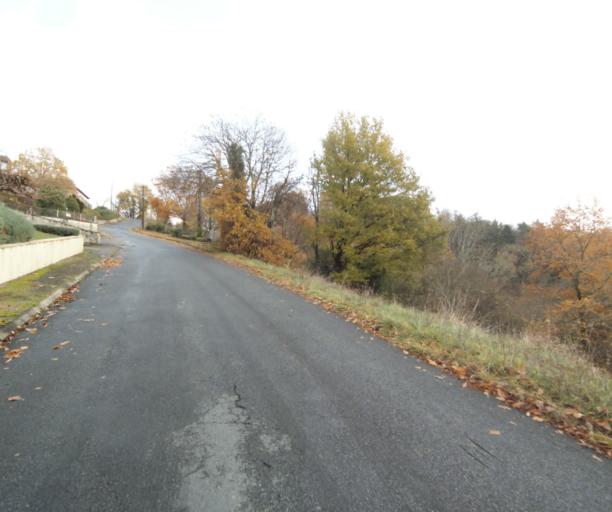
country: FR
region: Limousin
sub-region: Departement de la Correze
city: Cornil
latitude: 45.2060
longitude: 1.6935
